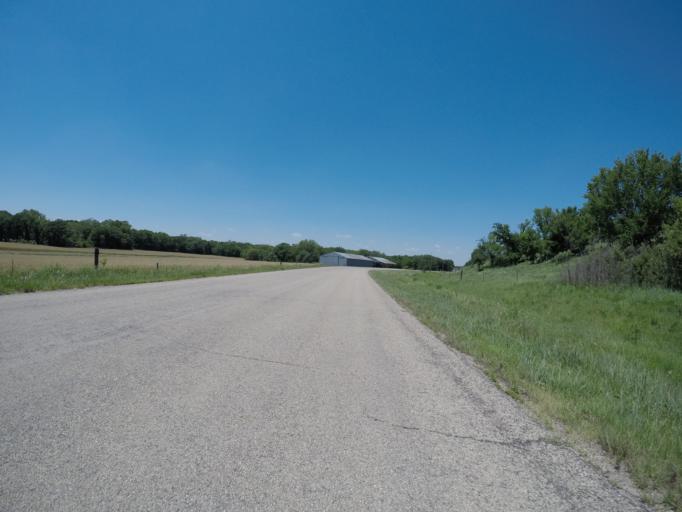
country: US
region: Kansas
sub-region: Geary County
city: Grandview Plaza
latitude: 38.8587
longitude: -96.7846
